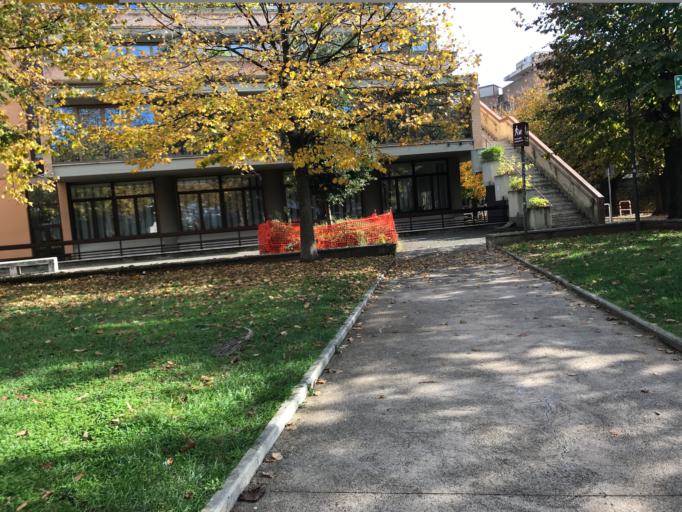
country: IT
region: Latium
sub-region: Citta metropolitana di Roma Capitale
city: Rome
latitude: 41.9034
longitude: 12.5165
